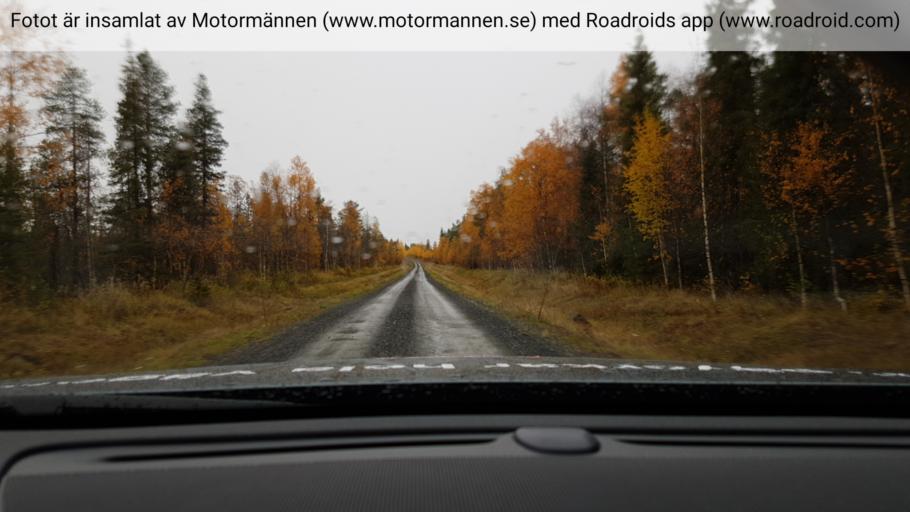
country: SE
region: Norrbotten
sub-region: Pajala Kommun
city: Pajala
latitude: 67.0317
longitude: 22.8492
